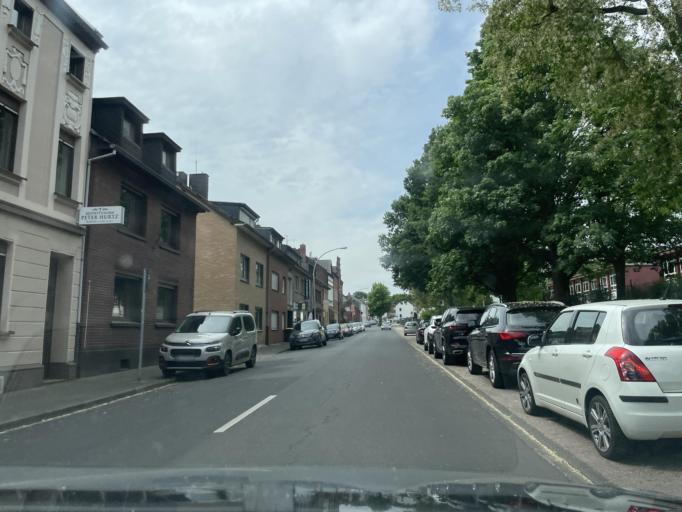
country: DE
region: North Rhine-Westphalia
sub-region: Regierungsbezirk Dusseldorf
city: Monchengladbach
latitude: 51.1516
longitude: 6.4193
